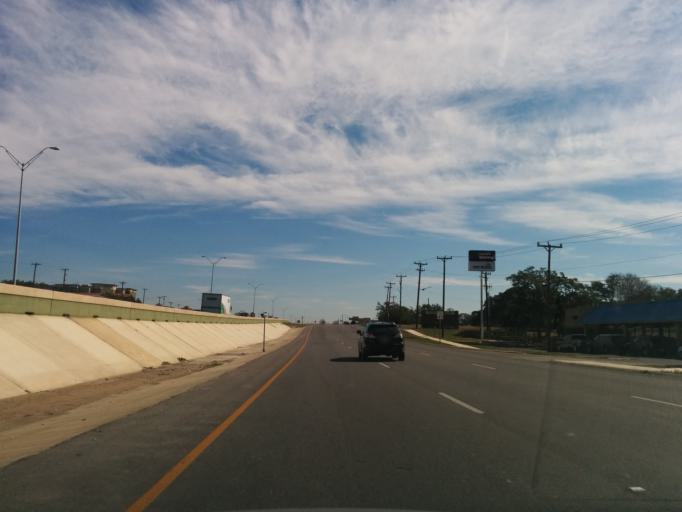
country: US
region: Texas
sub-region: Bexar County
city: Hollywood Park
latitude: 29.6091
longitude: -98.4866
